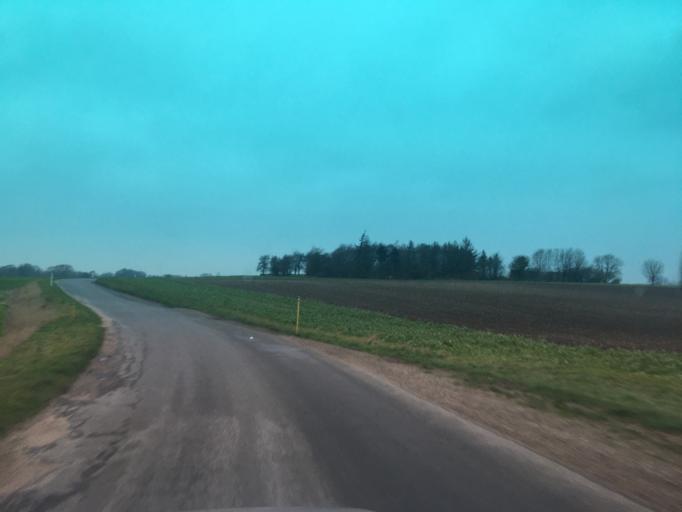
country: DK
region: Zealand
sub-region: Naestved Kommune
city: Fuglebjerg
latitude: 55.2820
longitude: 11.4370
